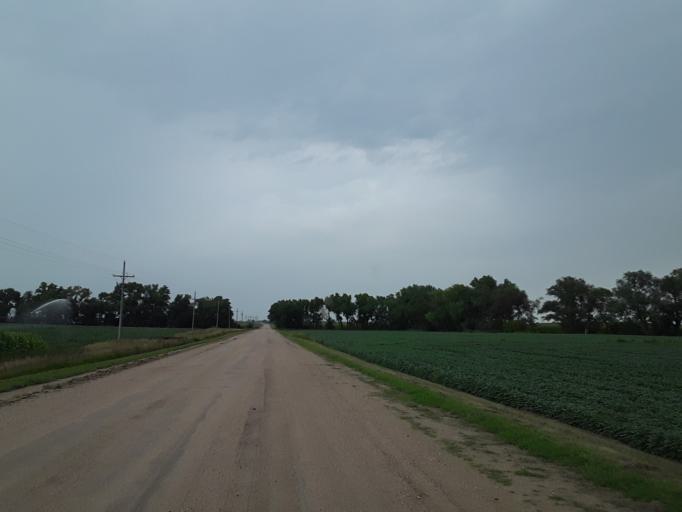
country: US
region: Nebraska
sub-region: Saunders County
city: Yutan
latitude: 41.1638
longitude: -96.4448
